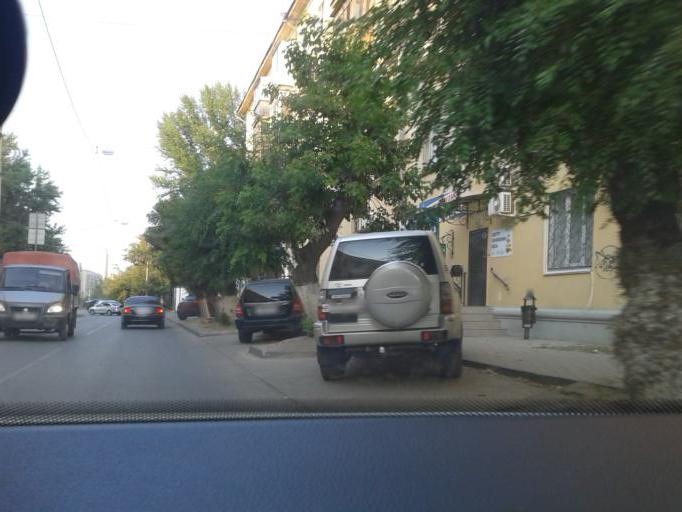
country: RU
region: Volgograd
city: Volgograd
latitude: 48.6984
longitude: 44.5070
